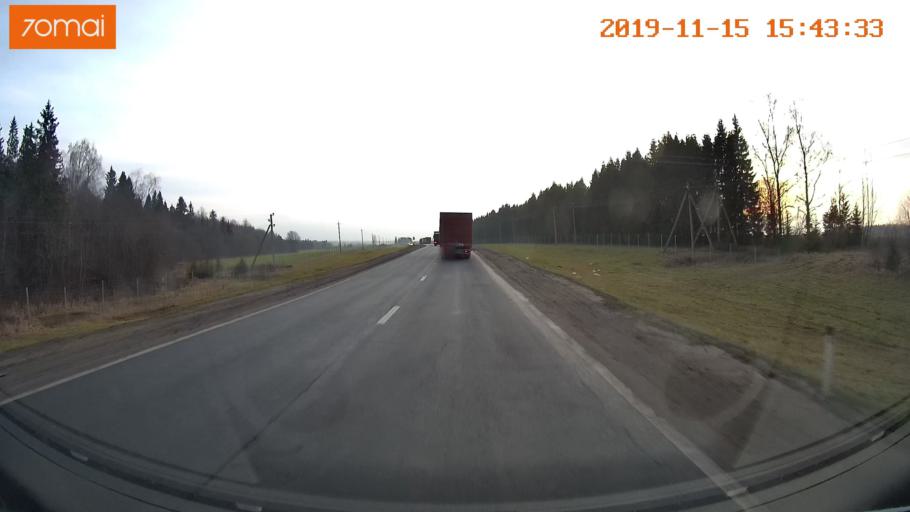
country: RU
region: Jaroslavl
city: Danilov
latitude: 57.9810
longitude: 40.0268
